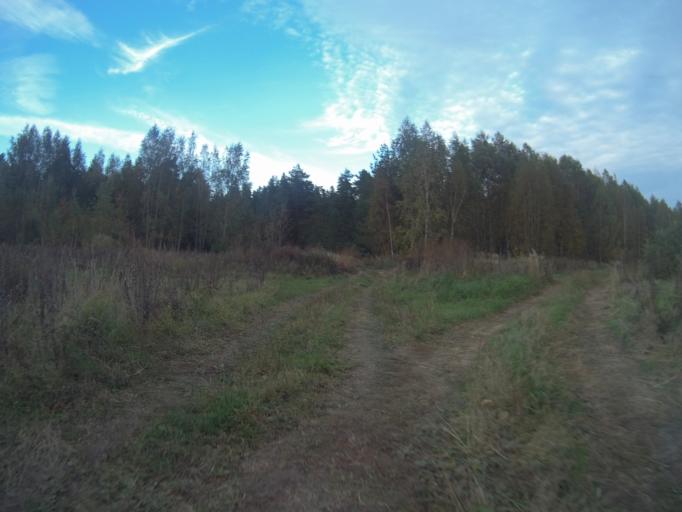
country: RU
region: Vladimir
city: Raduzhnyy
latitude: 56.0188
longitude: 40.3735
